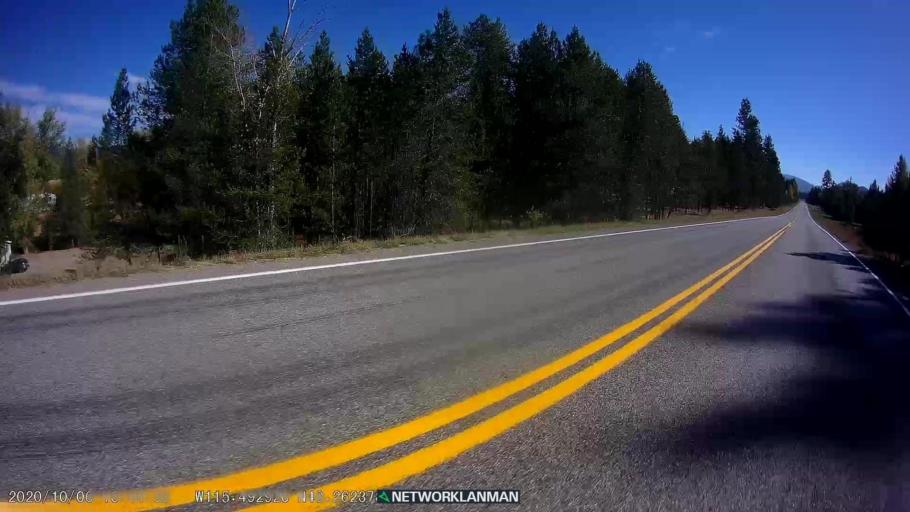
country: US
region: Montana
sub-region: Lincoln County
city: Libby
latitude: 48.2621
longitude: -115.4928
